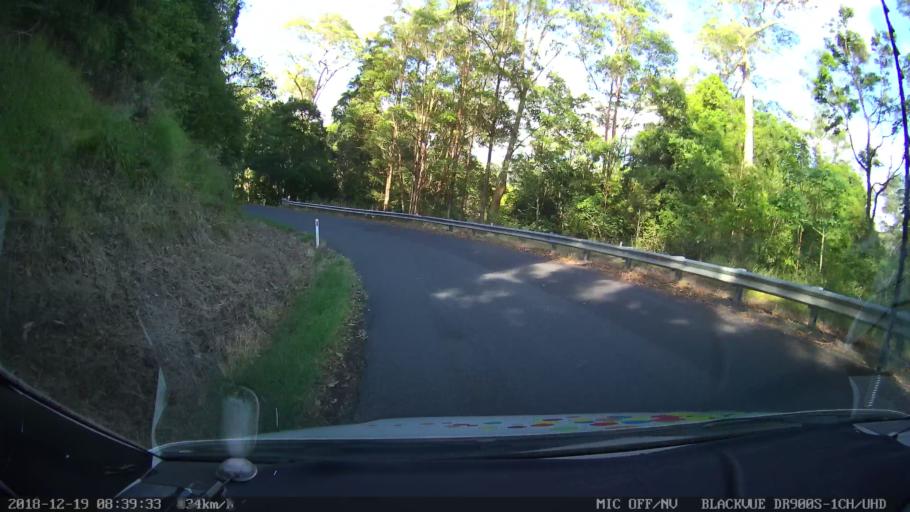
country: AU
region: New South Wales
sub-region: Kyogle
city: Kyogle
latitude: -28.3366
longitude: 152.9714
